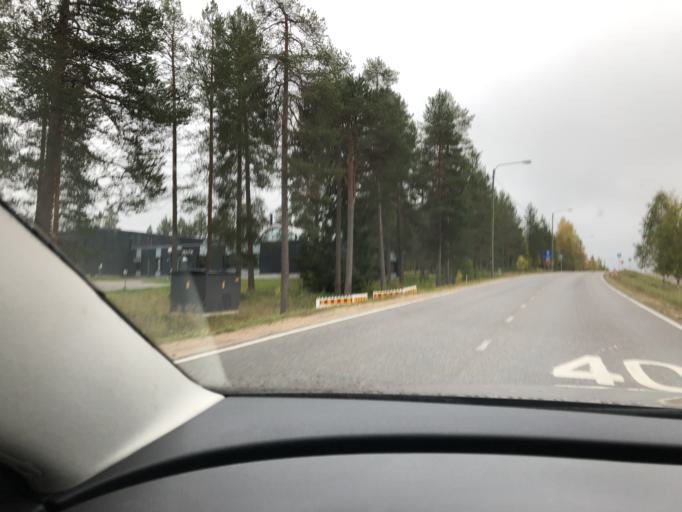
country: FI
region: Lapland
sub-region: Itae-Lappi
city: Posio
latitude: 66.1136
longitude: 28.1816
